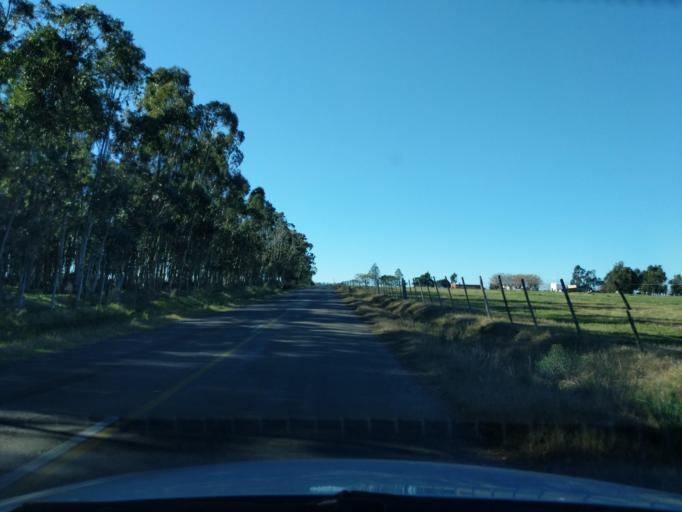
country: UY
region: Florida
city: Florida
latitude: -34.0513
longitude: -56.2490
